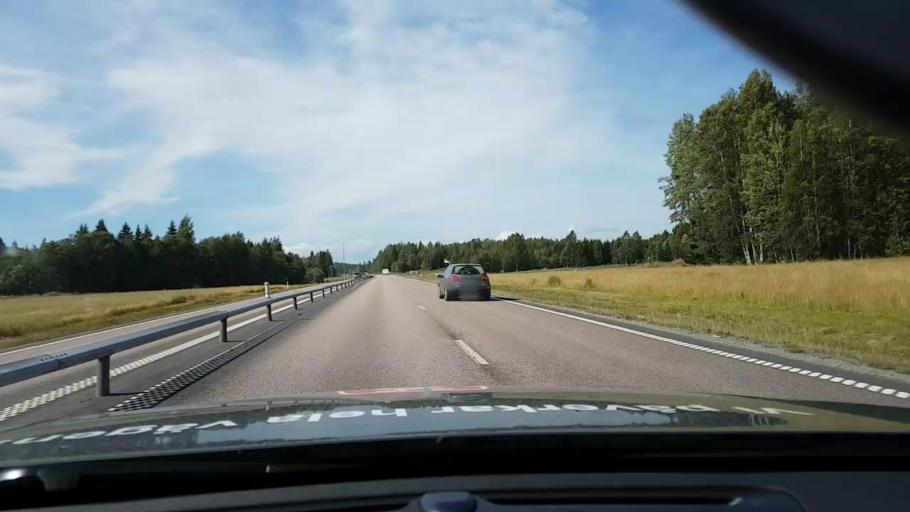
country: SE
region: Vaesternorrland
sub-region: OErnskoeldsviks Kommun
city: Ornskoldsvik
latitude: 63.3005
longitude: 18.8636
